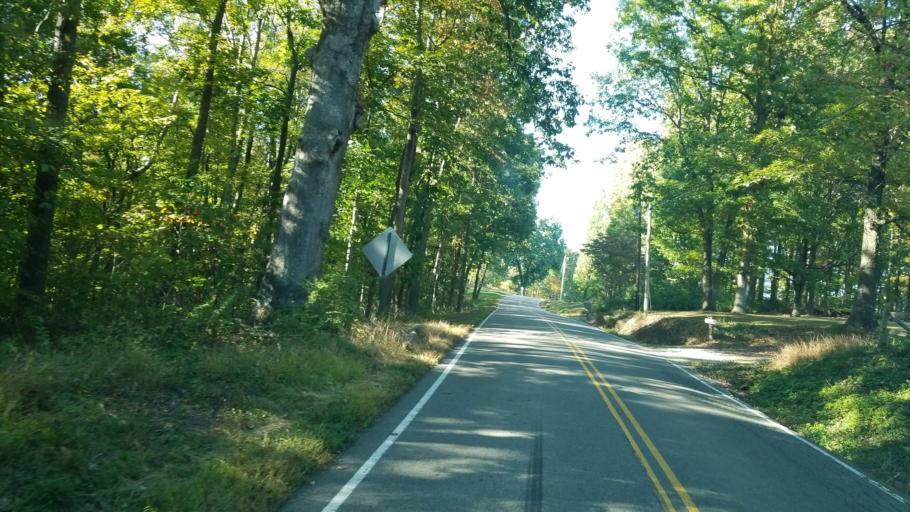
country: US
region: Ohio
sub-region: Licking County
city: Utica
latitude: 40.1653
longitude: -82.3780
